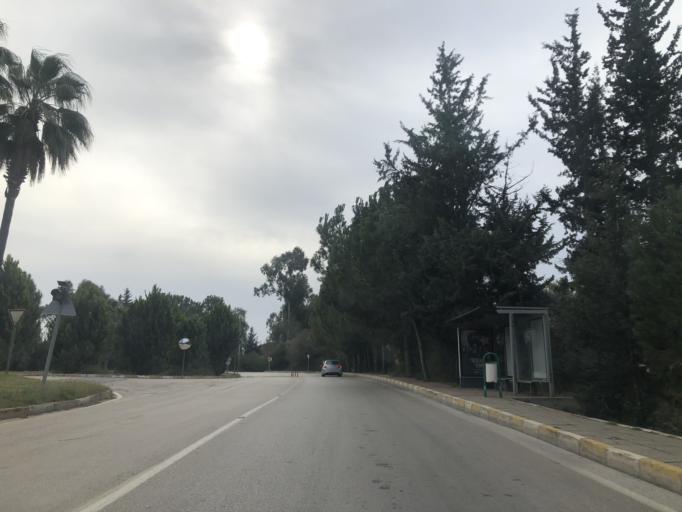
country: TR
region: Adana
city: Adana
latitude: 37.0572
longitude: 35.3540
